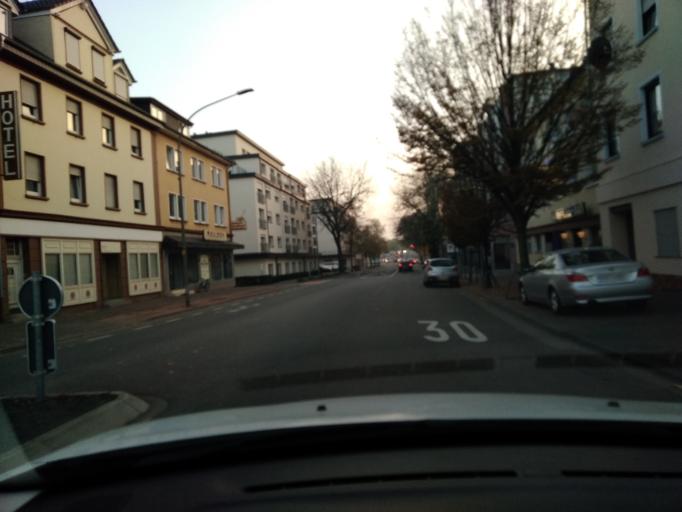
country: DE
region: Saarland
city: Saarlouis
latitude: 49.3270
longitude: 6.7496
